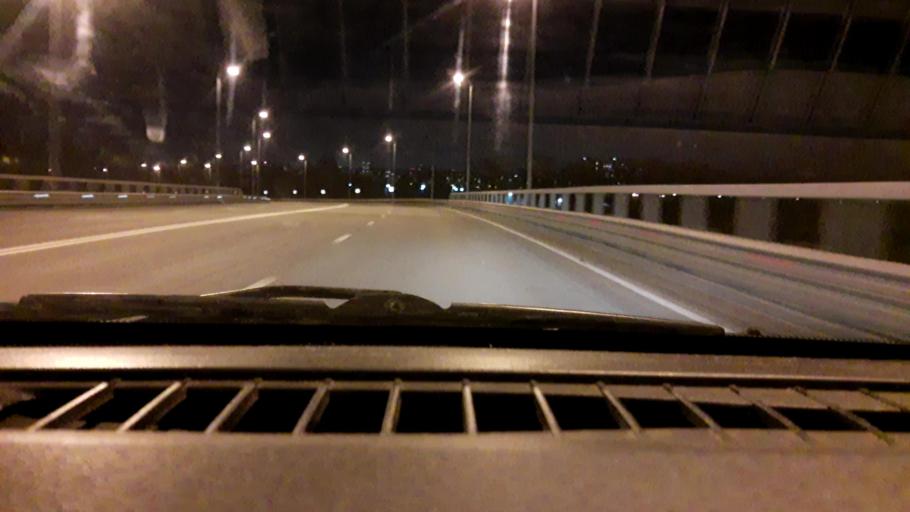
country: RU
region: Nizjnij Novgorod
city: Gorbatovka
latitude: 56.2284
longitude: 43.8058
